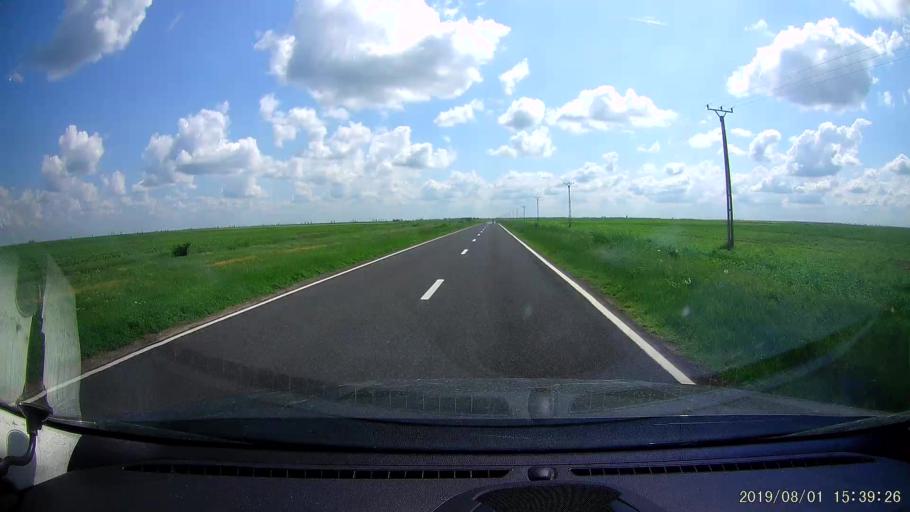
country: RO
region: Braila
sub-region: Comuna Victoria
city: Victoria
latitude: 44.8577
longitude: 27.5597
